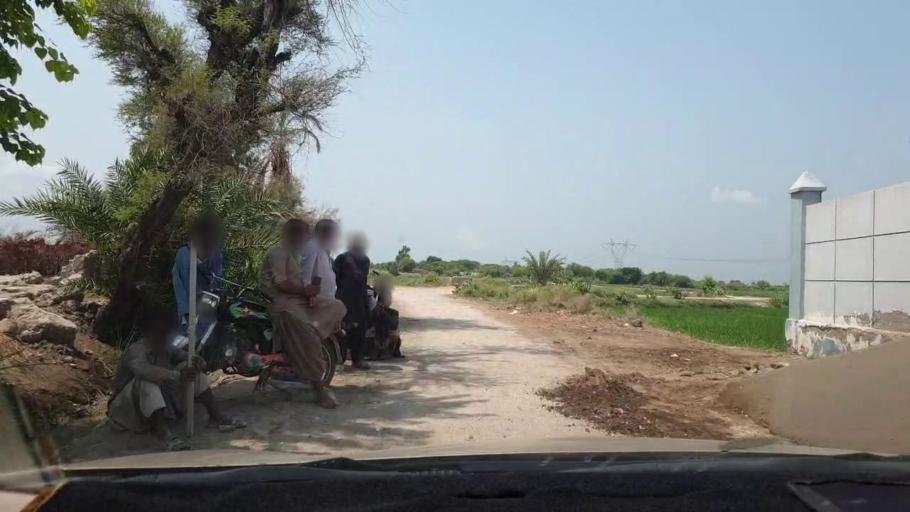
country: PK
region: Sindh
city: Naudero
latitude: 27.6643
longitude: 68.3069
